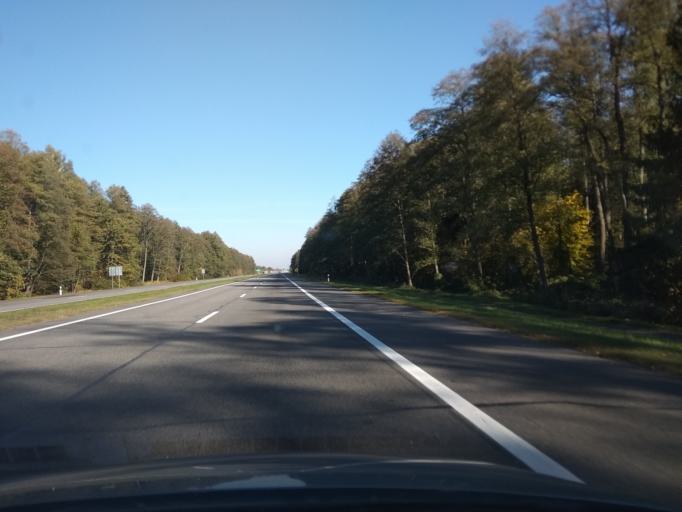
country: BY
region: Brest
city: Ivatsevichy
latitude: 52.6880
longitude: 25.3415
